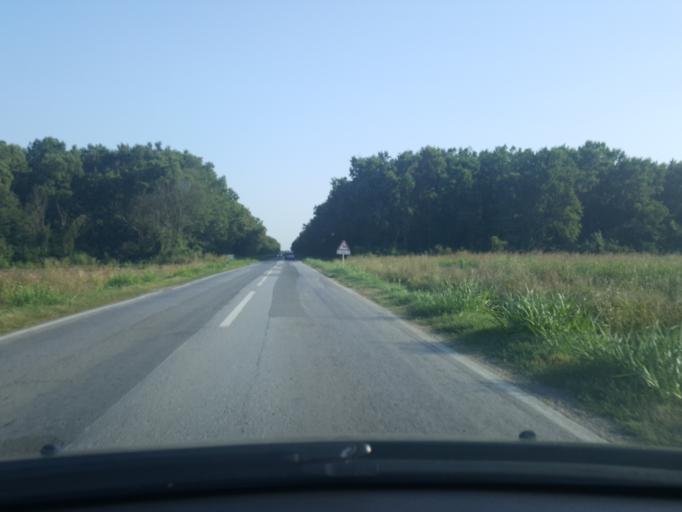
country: RS
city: Jarak
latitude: 44.9051
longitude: 19.7646
